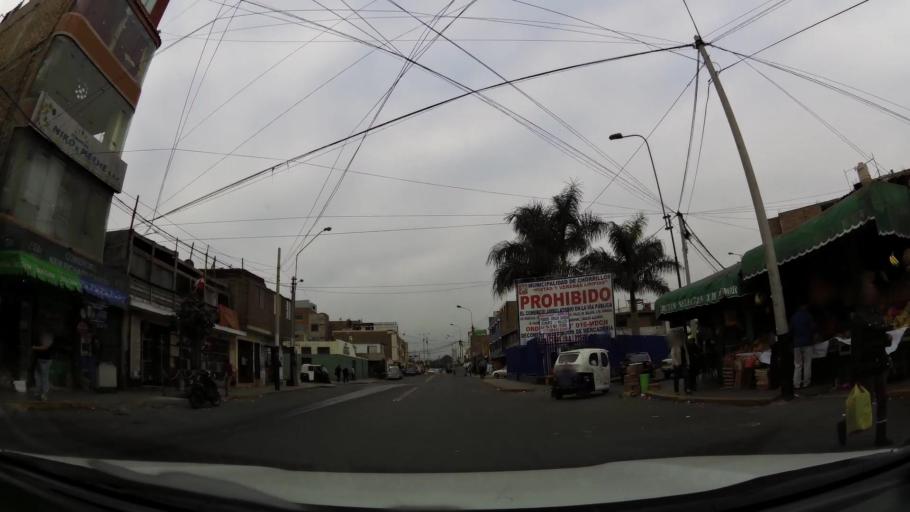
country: PE
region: Lima
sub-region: Lima
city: Surco
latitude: -12.1680
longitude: -77.0210
